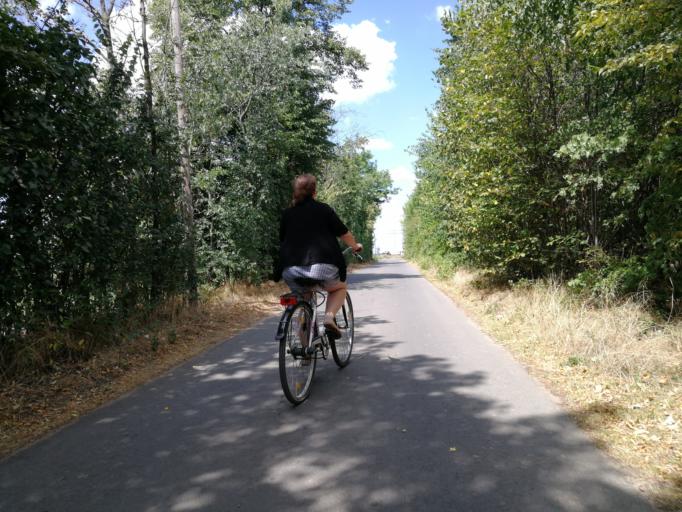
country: DE
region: North Rhine-Westphalia
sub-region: Regierungsbezirk Dusseldorf
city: Dormagen
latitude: 51.0944
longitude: 6.7772
